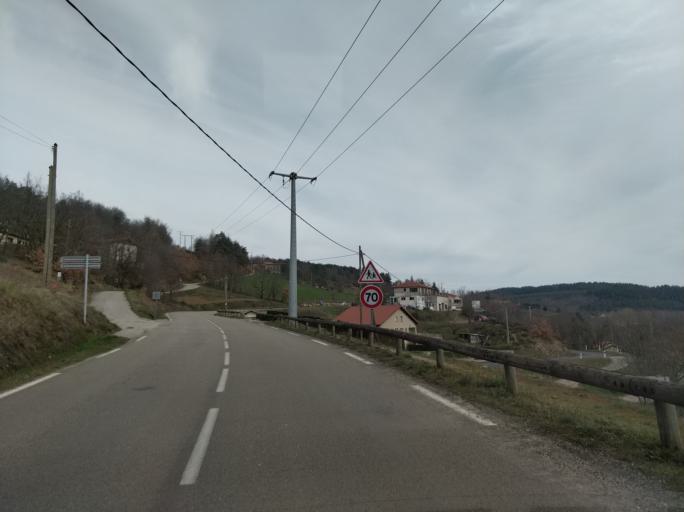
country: FR
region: Rhone-Alpes
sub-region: Departement de l'Ardeche
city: Satillieu
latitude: 45.1586
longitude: 4.6317
